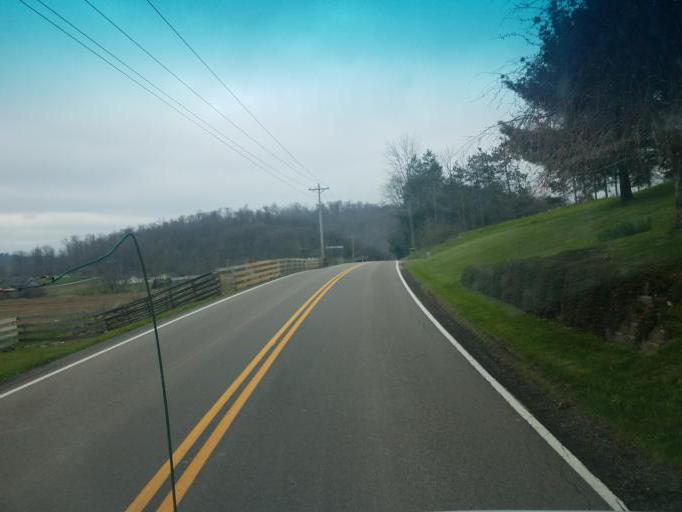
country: US
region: Ohio
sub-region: Stark County
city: Beach City
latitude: 40.6050
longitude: -81.6666
